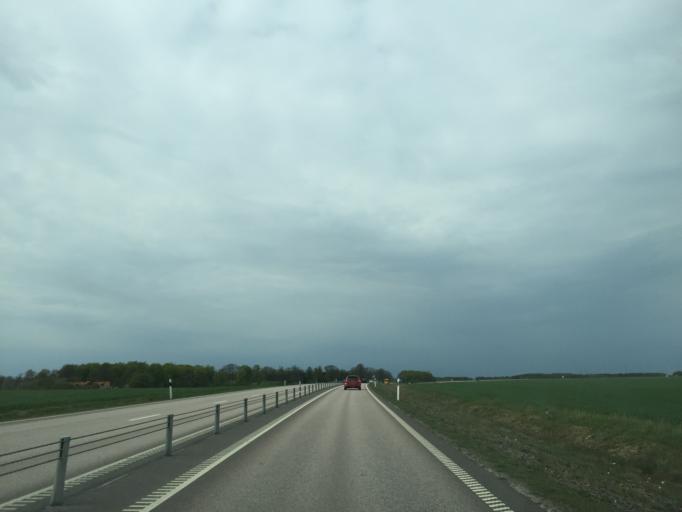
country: SE
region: Skane
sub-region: Helsingborg
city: Helsingborg
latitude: 56.1093
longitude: 12.6485
